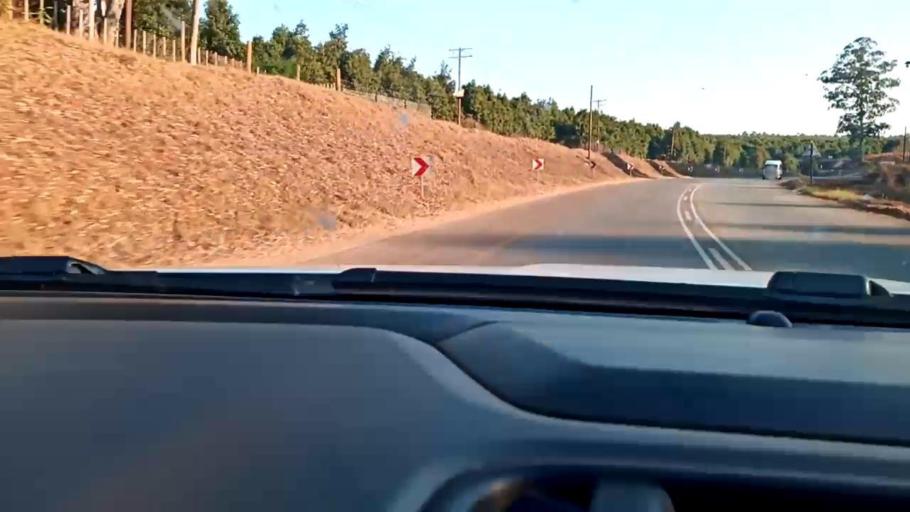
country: ZA
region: Limpopo
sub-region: Mopani District Municipality
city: Duiwelskloof
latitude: -23.7109
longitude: 30.1296
